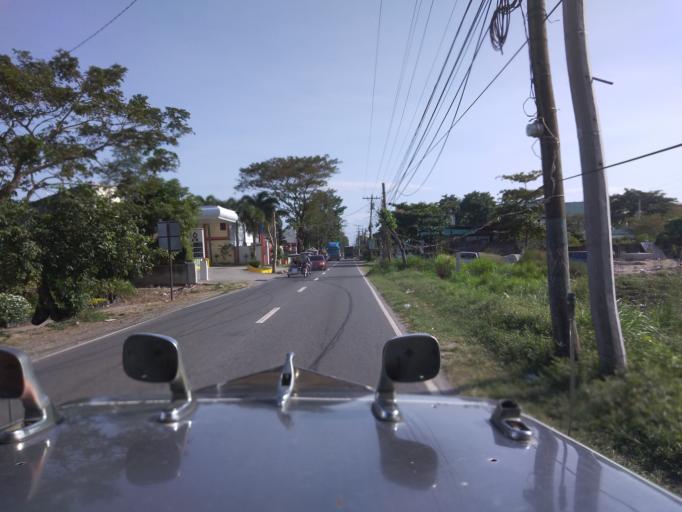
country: PH
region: Central Luzon
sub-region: Province of Pampanga
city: Arenas
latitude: 15.1730
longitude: 120.6804
